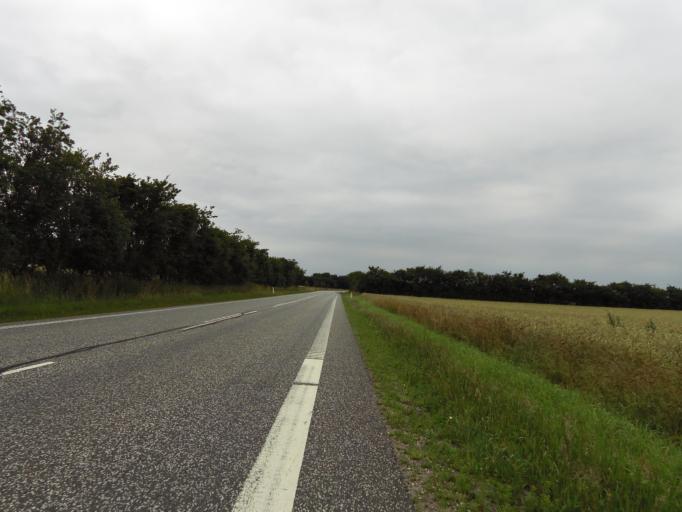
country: DK
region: South Denmark
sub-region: Tonder Kommune
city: Logumkloster
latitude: 55.1048
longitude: 8.9435
